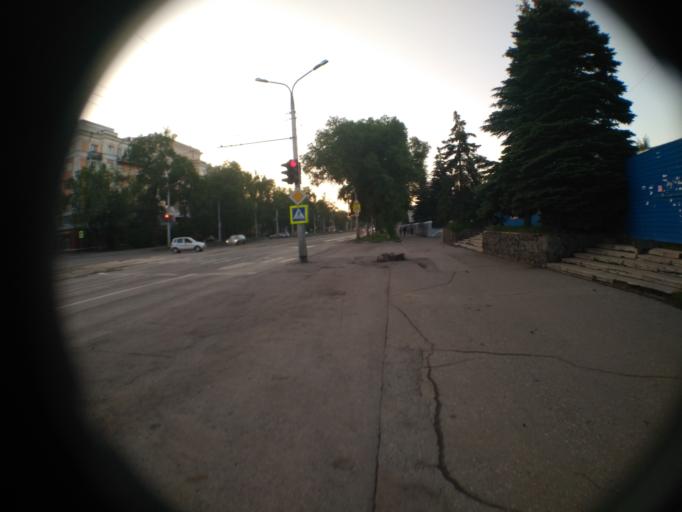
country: RU
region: Kemerovo
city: Novokuznetsk
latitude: 53.7543
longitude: 87.1185
